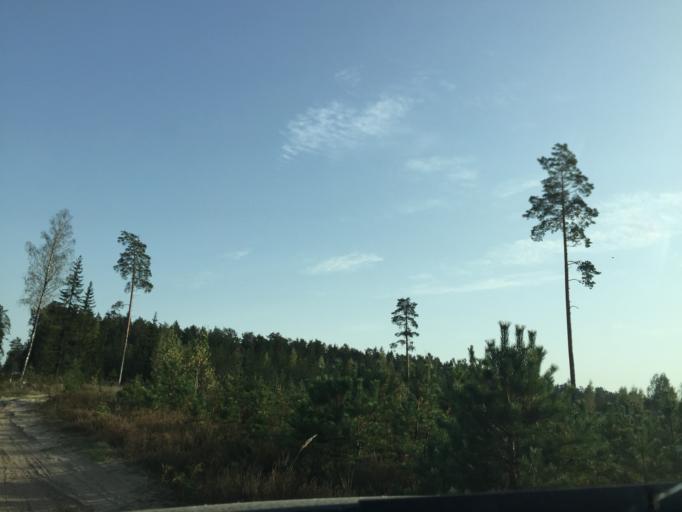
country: LV
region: Garkalne
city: Garkalne
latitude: 56.9676
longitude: 24.4213
